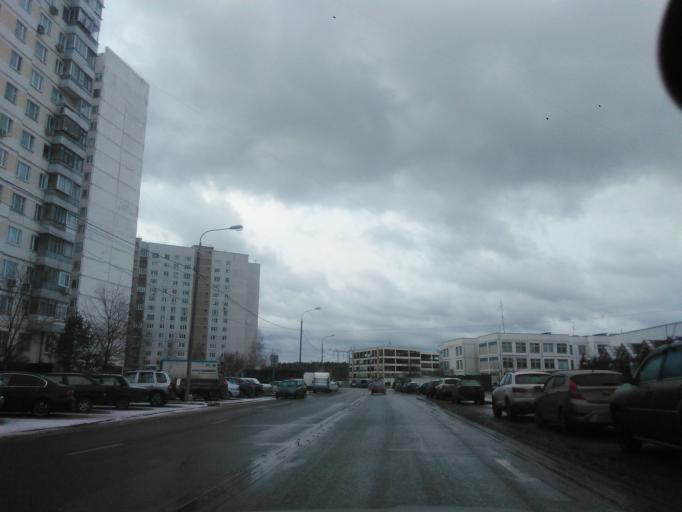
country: RU
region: Moskovskaya
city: Krasnogorsk
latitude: 55.8592
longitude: 37.3447
